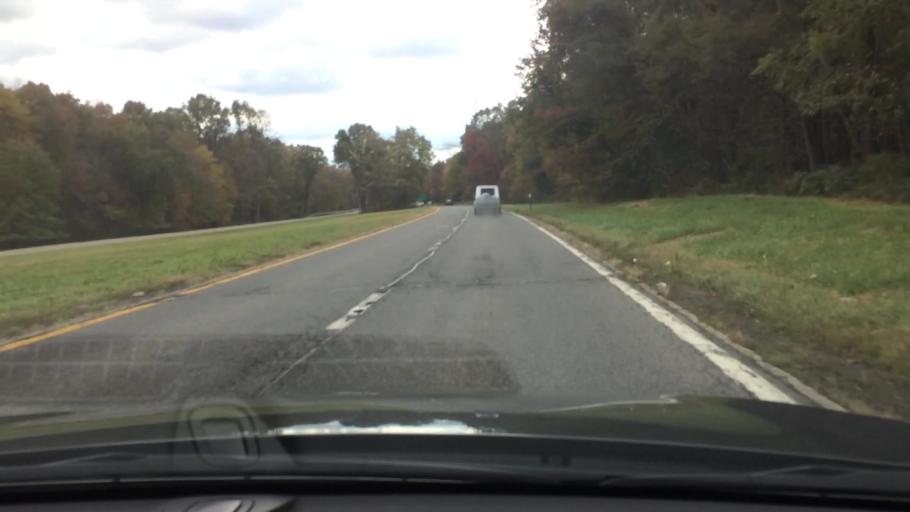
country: US
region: New York
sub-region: Dutchess County
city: Hillside Lake
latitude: 41.6038
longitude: -73.7636
